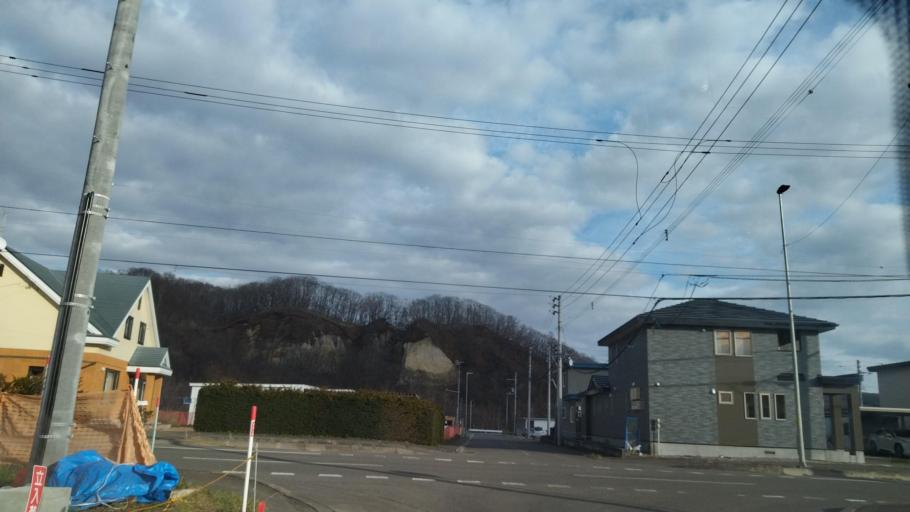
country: JP
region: Hokkaido
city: Otofuke
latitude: 43.2467
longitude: 143.5527
